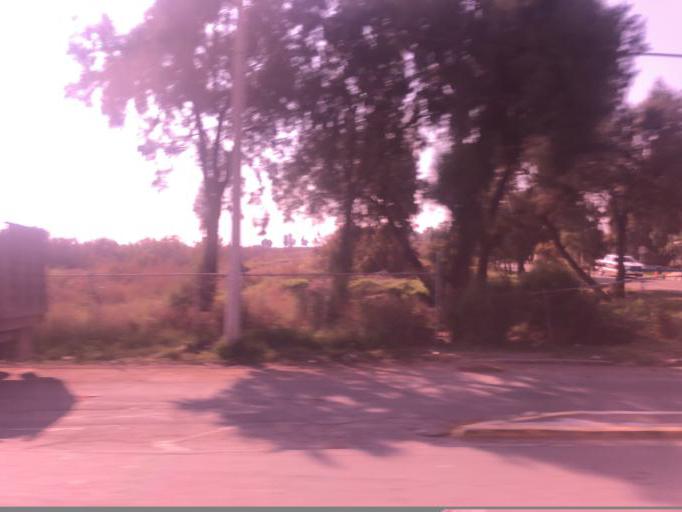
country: MX
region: Mexico
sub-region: Texcoco
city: Colonia Guadalupe Victoria
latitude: 19.4807
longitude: -98.9724
